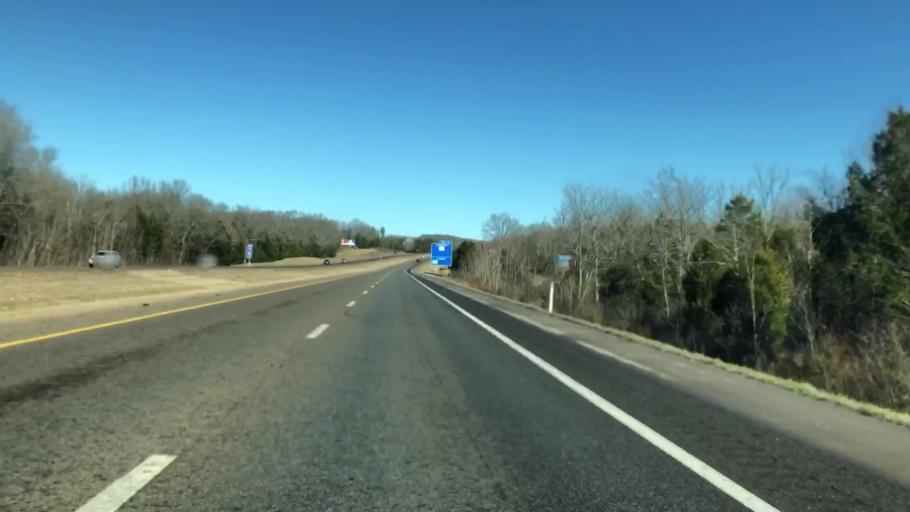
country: US
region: Tennessee
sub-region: Maury County
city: Columbia
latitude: 35.6148
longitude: -86.9001
